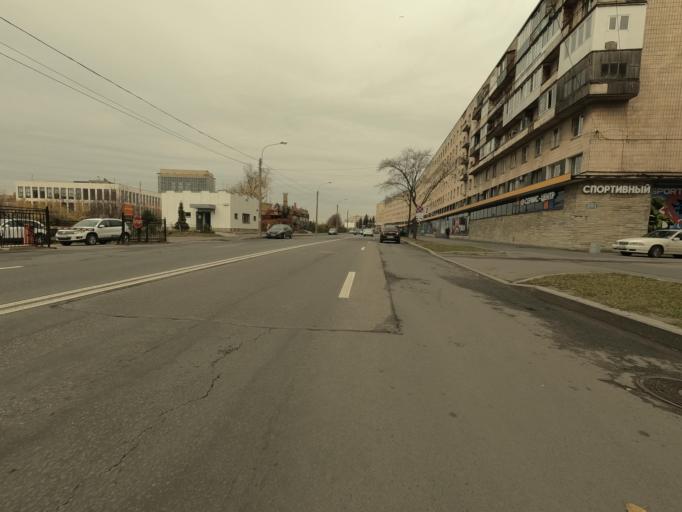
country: RU
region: St.-Petersburg
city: Centralniy
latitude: 59.9396
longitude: 30.4145
